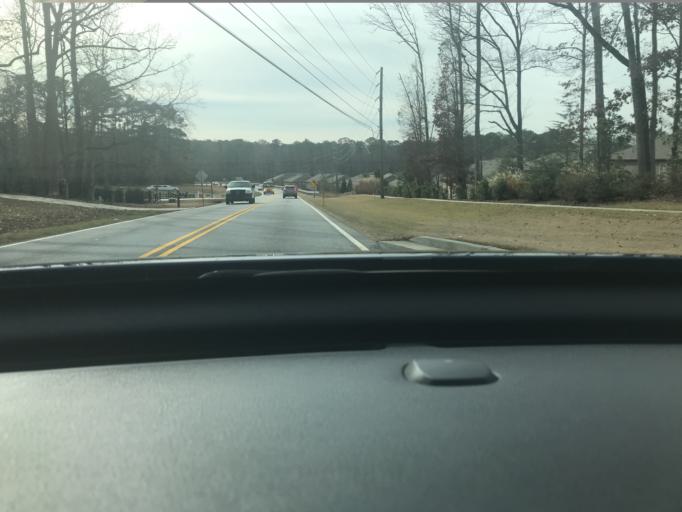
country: US
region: Georgia
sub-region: Gwinnett County
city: Mountain Park
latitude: 33.8662
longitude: -84.0959
